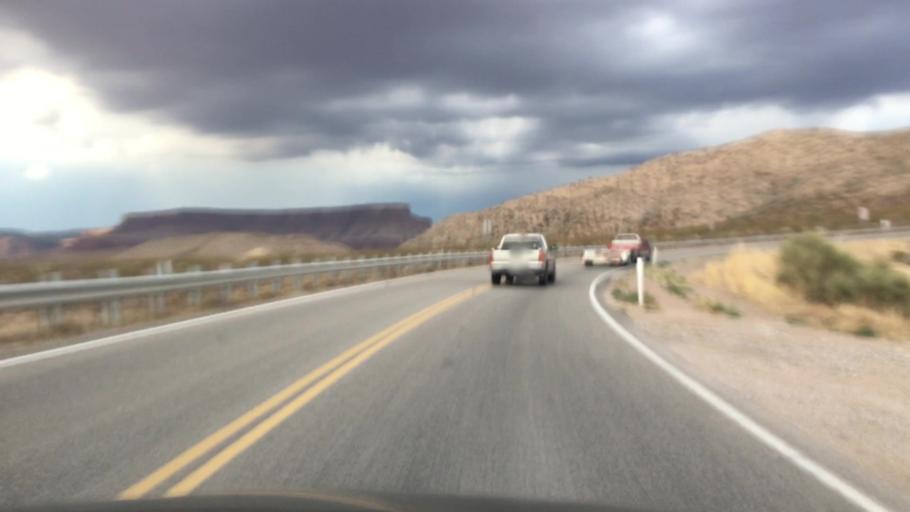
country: US
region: Utah
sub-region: Washington County
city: Hurricane
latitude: 37.1834
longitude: -113.2770
